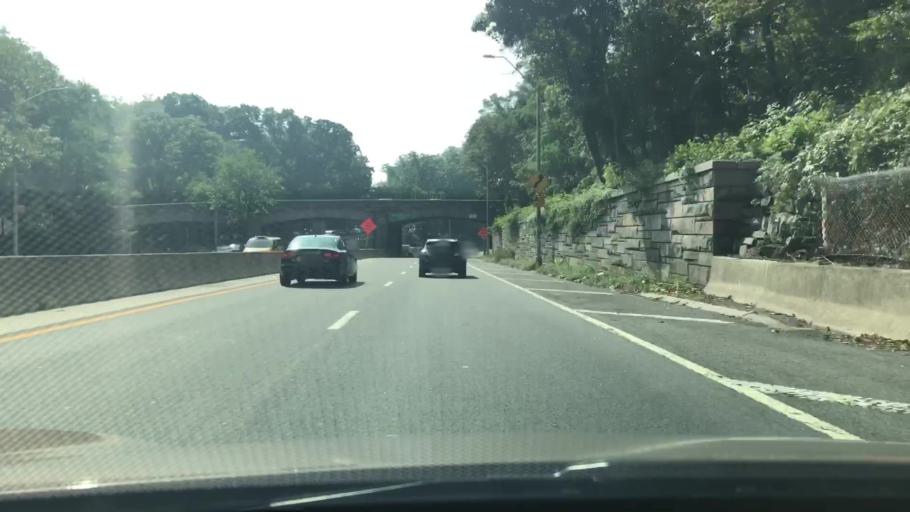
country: US
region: New York
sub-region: New York County
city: Inwood
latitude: 40.8915
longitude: -73.9083
